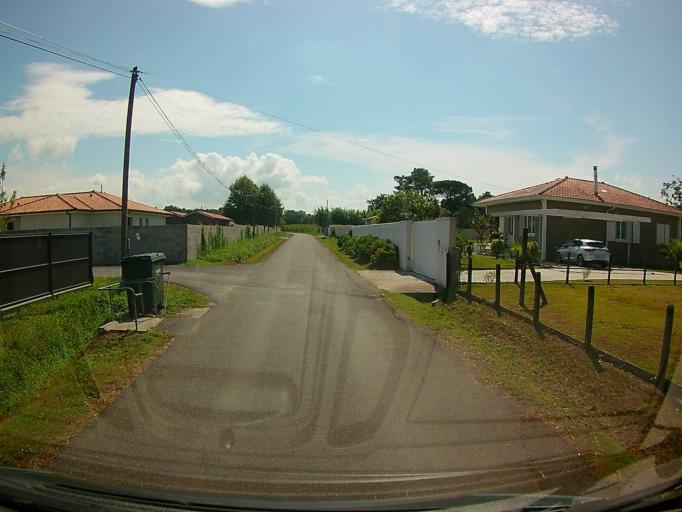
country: FR
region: Aquitaine
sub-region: Departement des Landes
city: Benesse-Maremne
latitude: 43.6271
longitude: -1.3816
